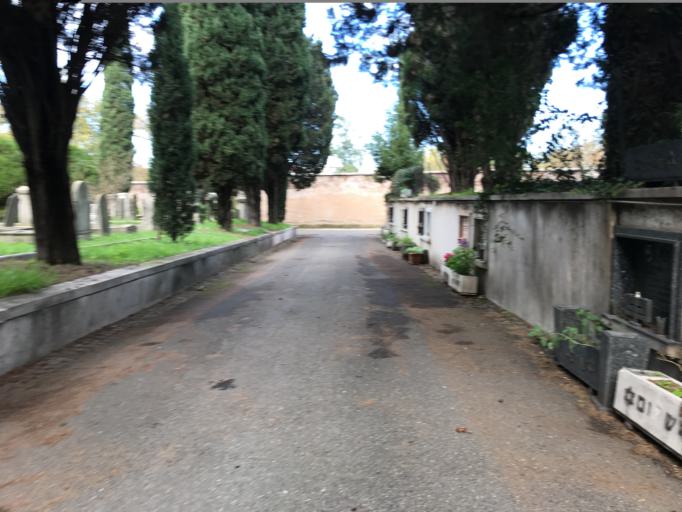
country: IT
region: Latium
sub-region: Citta metropolitana di Roma Capitale
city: Rome
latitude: 41.9077
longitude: 12.5292
